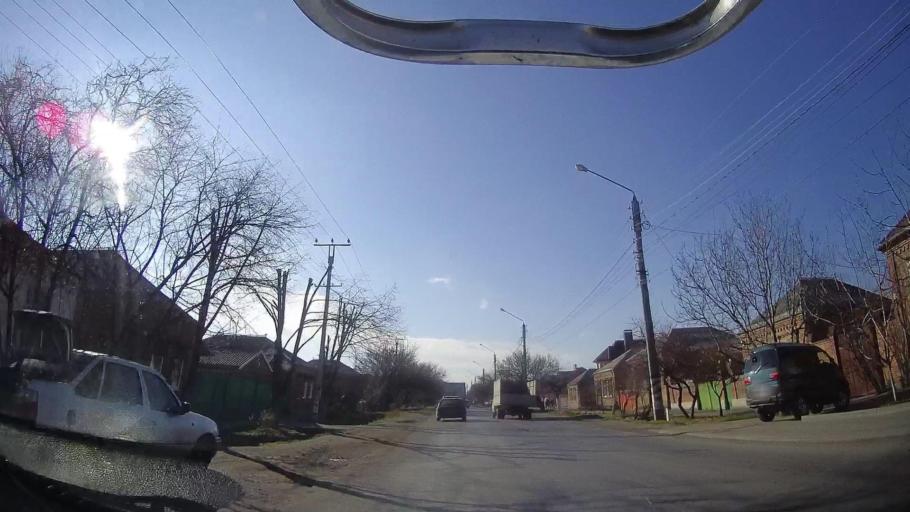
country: RU
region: Rostov
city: Bataysk
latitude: 47.1297
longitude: 39.6963
